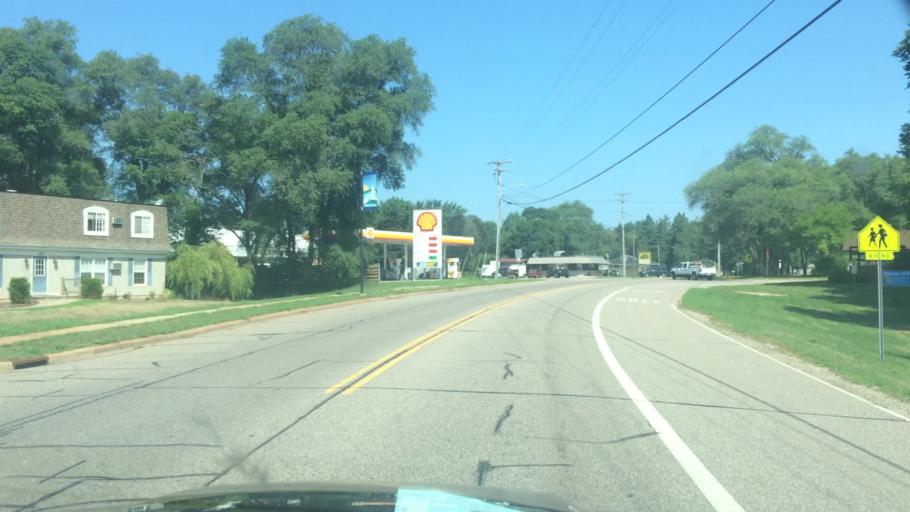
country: US
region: Wisconsin
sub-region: Waupaca County
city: Waupaca
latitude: 44.3454
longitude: -89.0718
